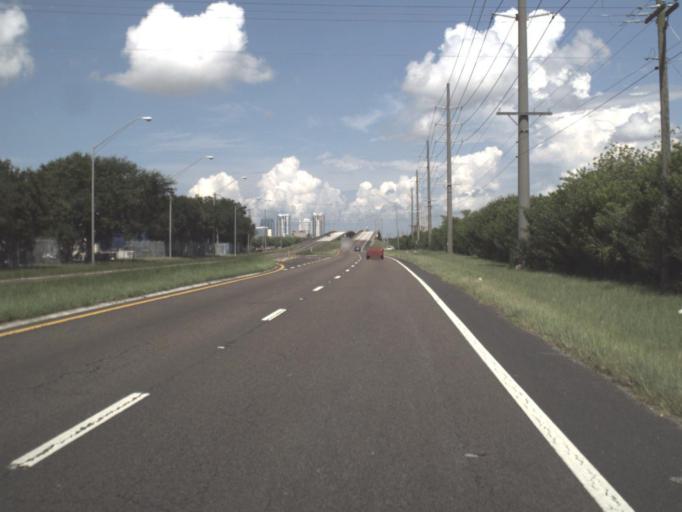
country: US
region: Florida
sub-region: Hillsborough County
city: Tampa
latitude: 27.9288
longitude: -82.4252
